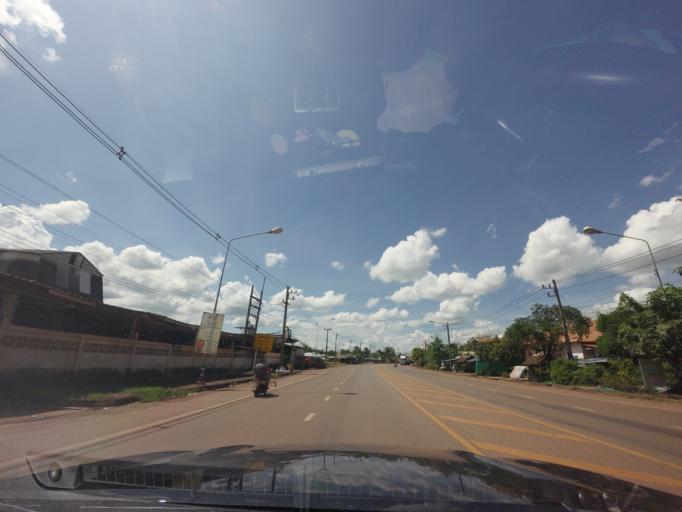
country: TH
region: Changwat Udon Thani
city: Ban Dung
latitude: 17.7044
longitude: 103.2532
